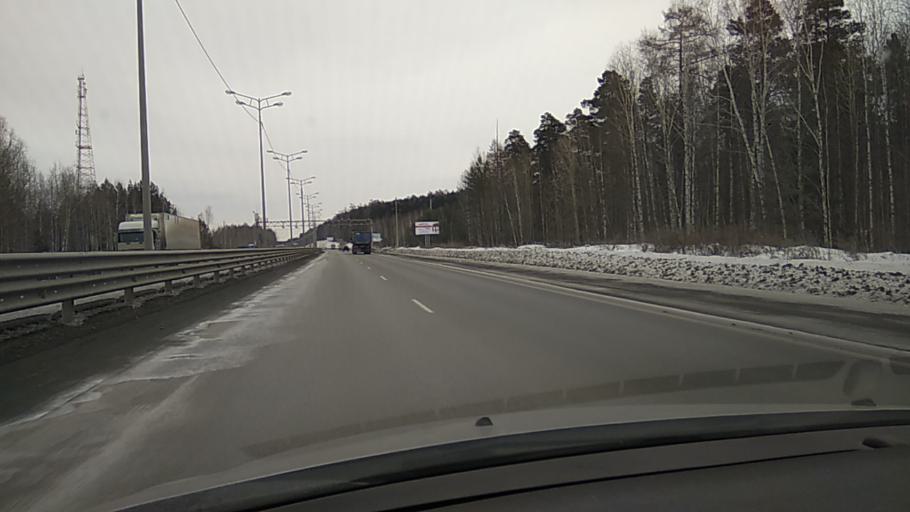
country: RU
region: Sverdlovsk
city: Severka
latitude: 56.8359
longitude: 60.2865
